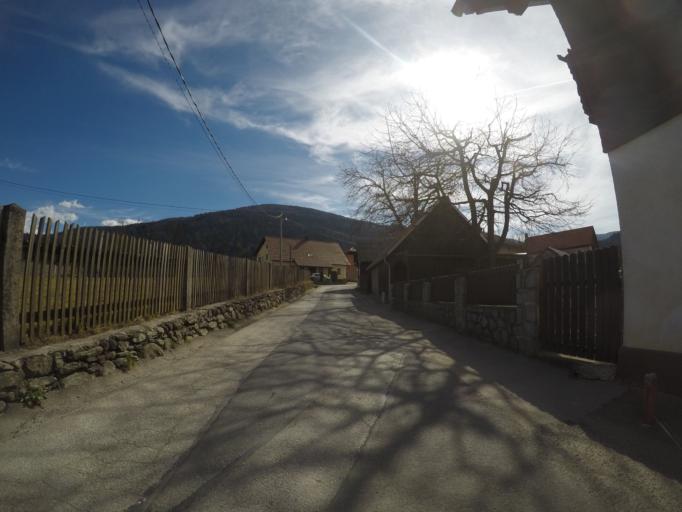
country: SI
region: Lovrenc na Pohorju
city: Lovrenc na Pohorju
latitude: 46.5359
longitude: 15.3850
